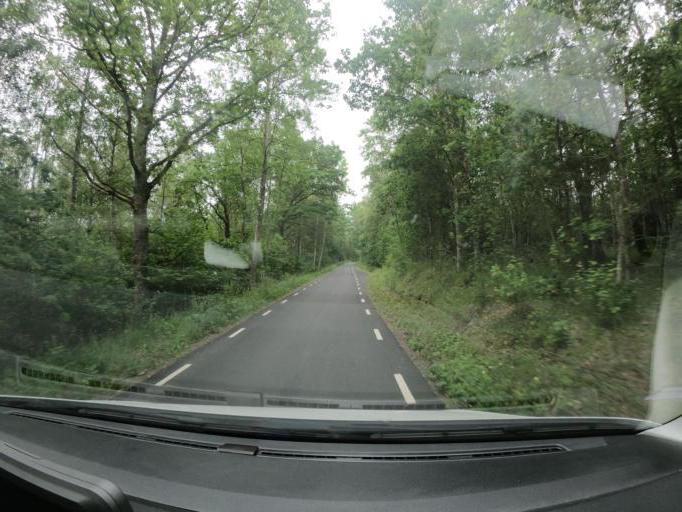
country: SE
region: Skane
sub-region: Perstorps Kommun
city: Perstorp
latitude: 56.0261
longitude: 13.3453
